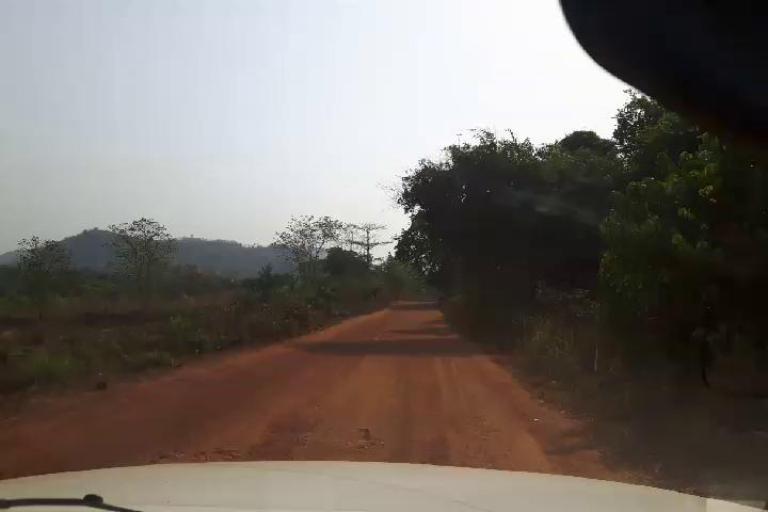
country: SL
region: Northern Province
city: Masingbi
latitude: 8.8587
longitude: -11.8188
